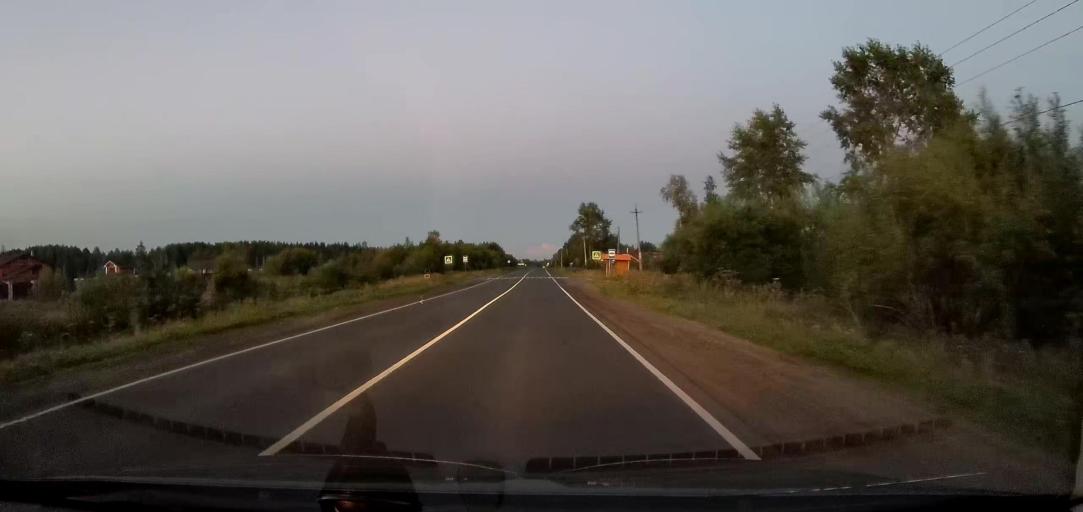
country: RU
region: Arkhangelskaya
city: Uyemskiy
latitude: 64.4467
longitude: 40.9475
